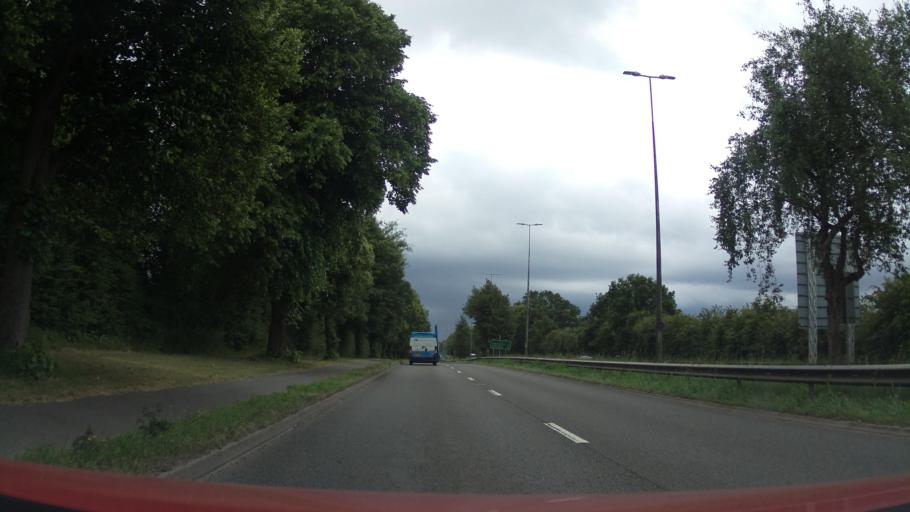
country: GB
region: England
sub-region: Staffordshire
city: Featherstone
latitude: 52.6521
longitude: -2.1295
